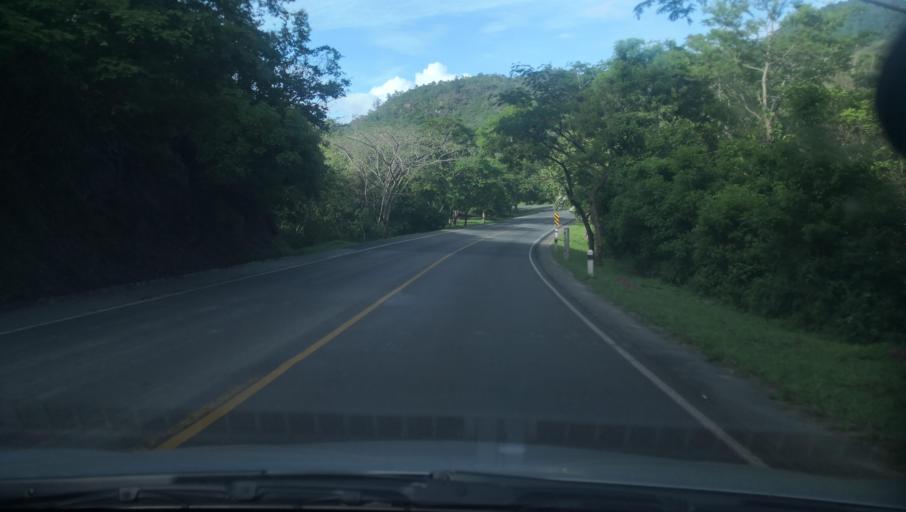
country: NI
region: Madriz
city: Totogalpa
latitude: 13.5763
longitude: -86.4785
